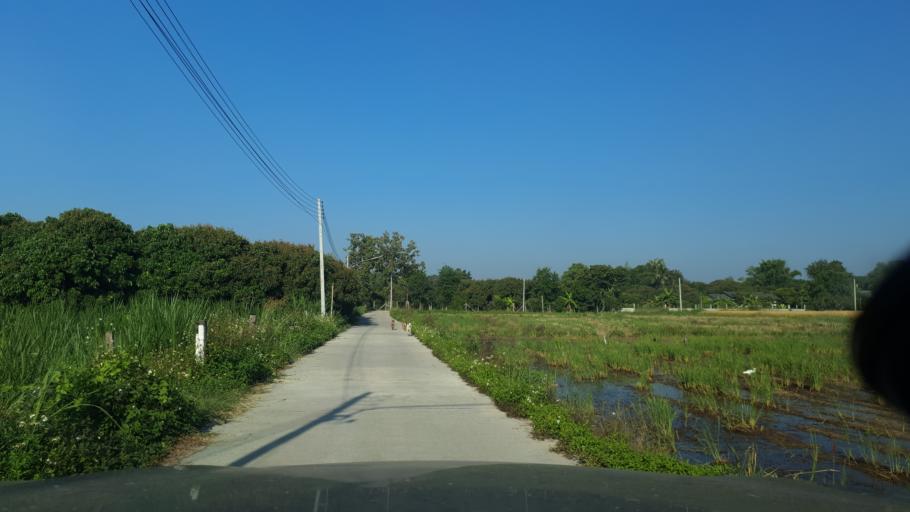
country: TH
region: Chiang Mai
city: San Kamphaeng
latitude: 18.6899
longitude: 99.1475
